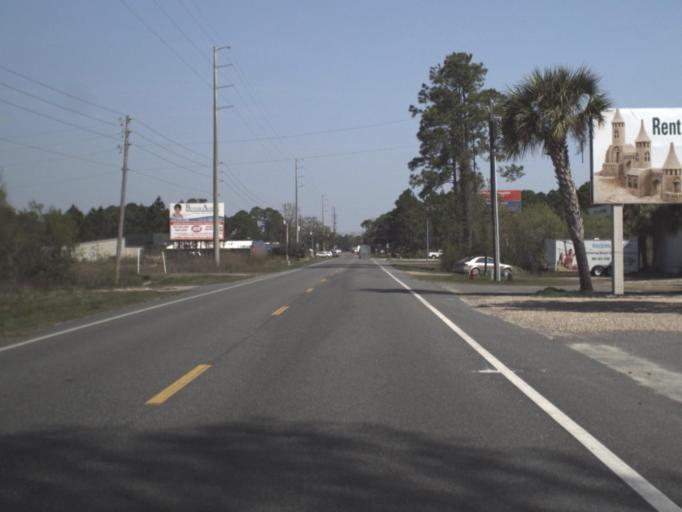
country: US
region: Florida
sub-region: Franklin County
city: Eastpoint
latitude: 29.7316
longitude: -84.8880
